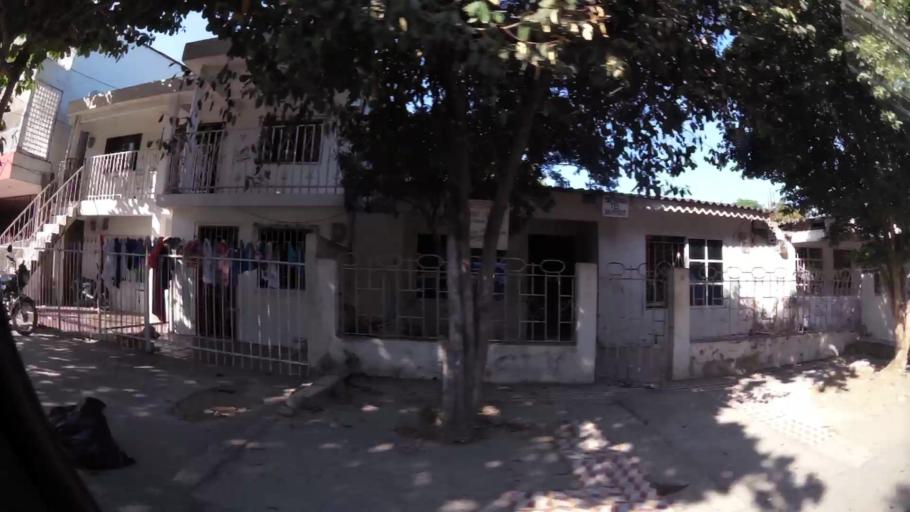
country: CO
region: Bolivar
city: Cartagena
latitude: 10.4058
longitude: -75.4924
